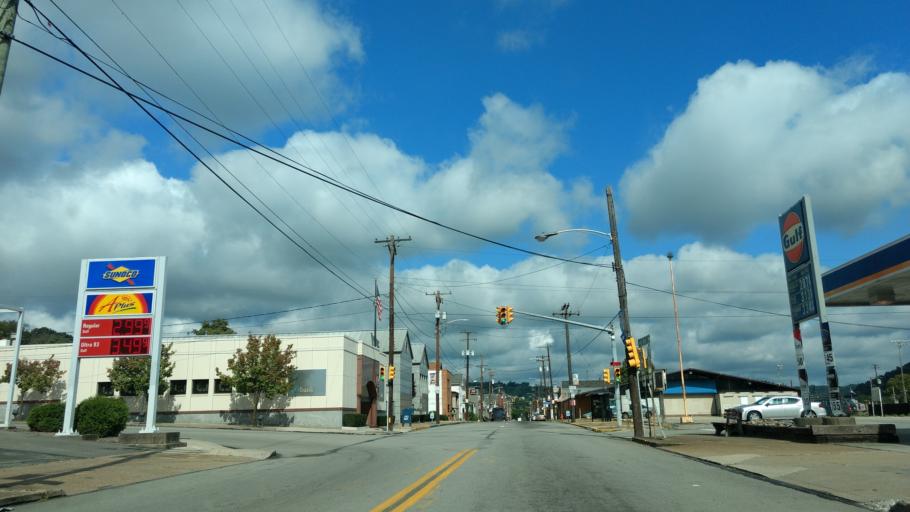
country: US
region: Pennsylvania
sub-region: Washington County
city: Charleroi
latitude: 40.1342
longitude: -79.8928
